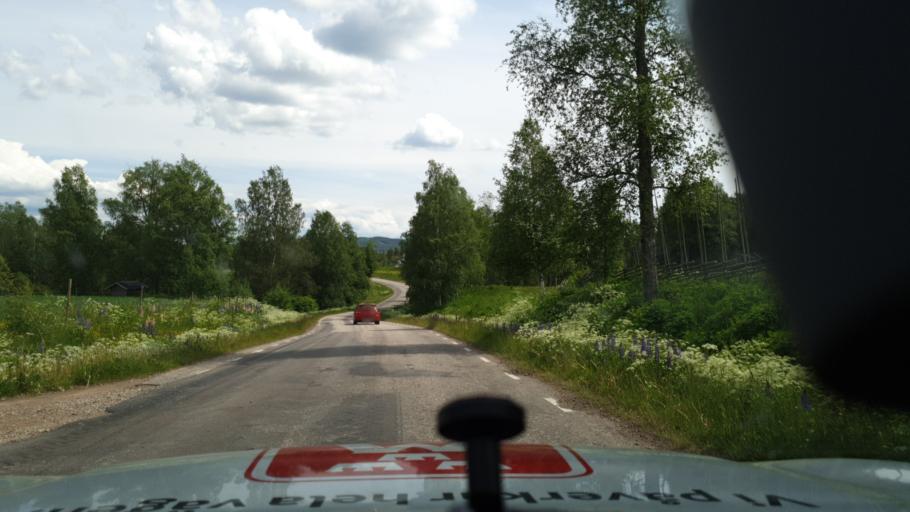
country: SE
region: Vaermland
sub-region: Torsby Kommun
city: Torsby
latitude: 59.9849
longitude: 12.8683
